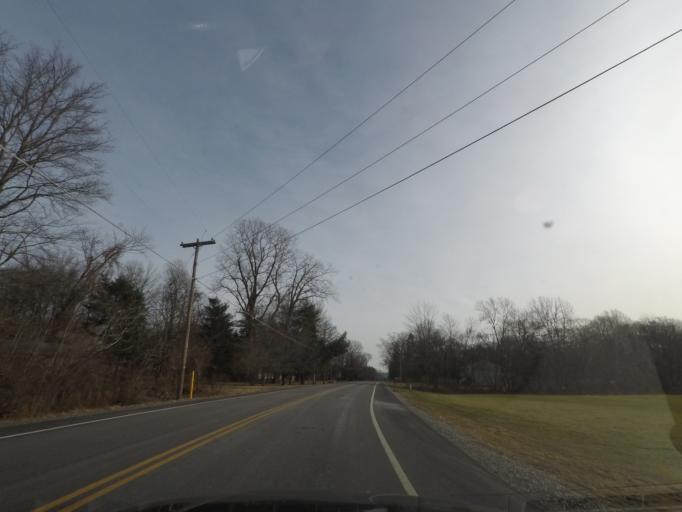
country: US
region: New York
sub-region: Saratoga County
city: Mechanicville
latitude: 42.8645
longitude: -73.6985
